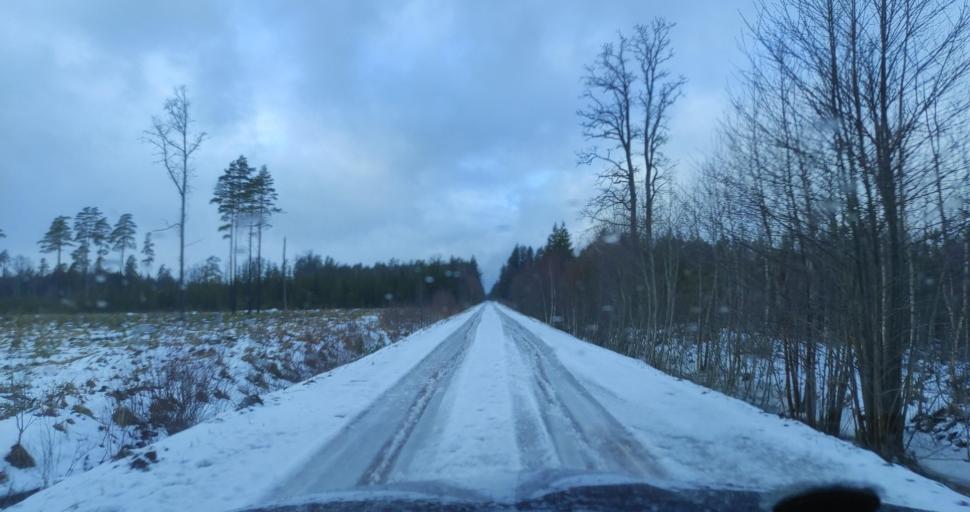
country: LV
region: Dundaga
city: Dundaga
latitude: 57.4089
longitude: 22.0866
